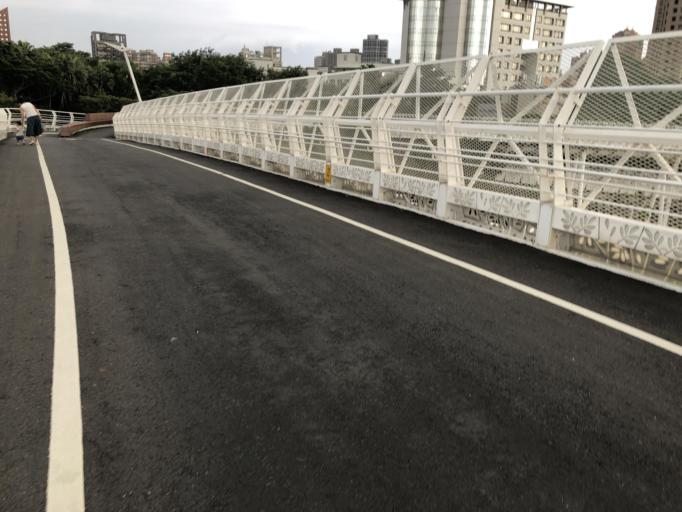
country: TW
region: Kaohsiung
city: Kaohsiung
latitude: 22.6795
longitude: 120.2989
